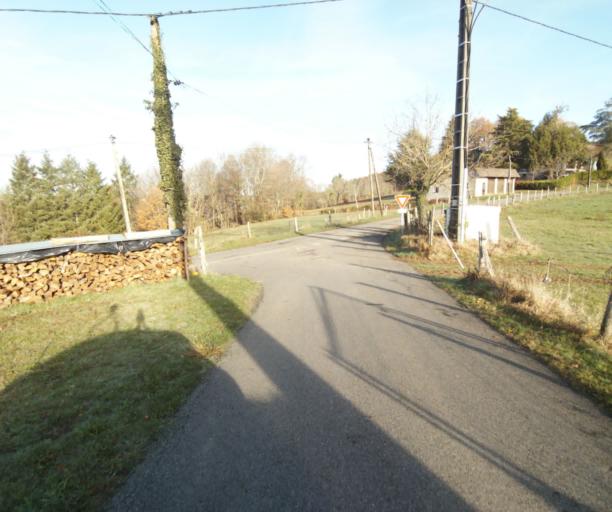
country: FR
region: Limousin
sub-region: Departement de la Correze
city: Laguenne
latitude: 45.2559
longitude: 1.7970
